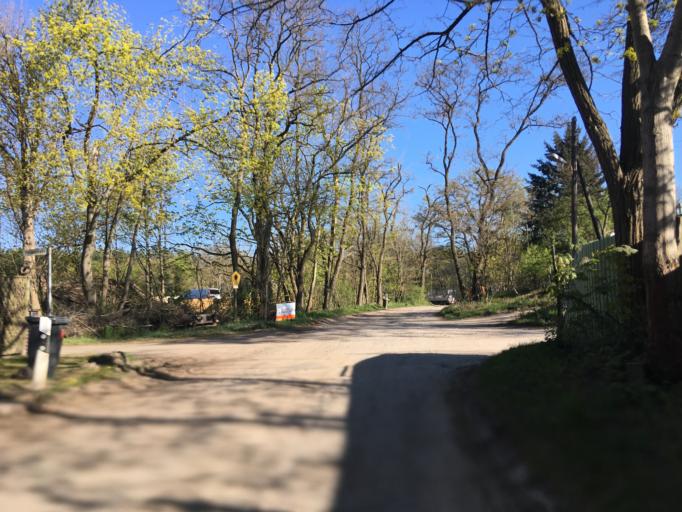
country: DE
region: Brandenburg
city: Bernau bei Berlin
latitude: 52.6934
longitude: 13.5488
